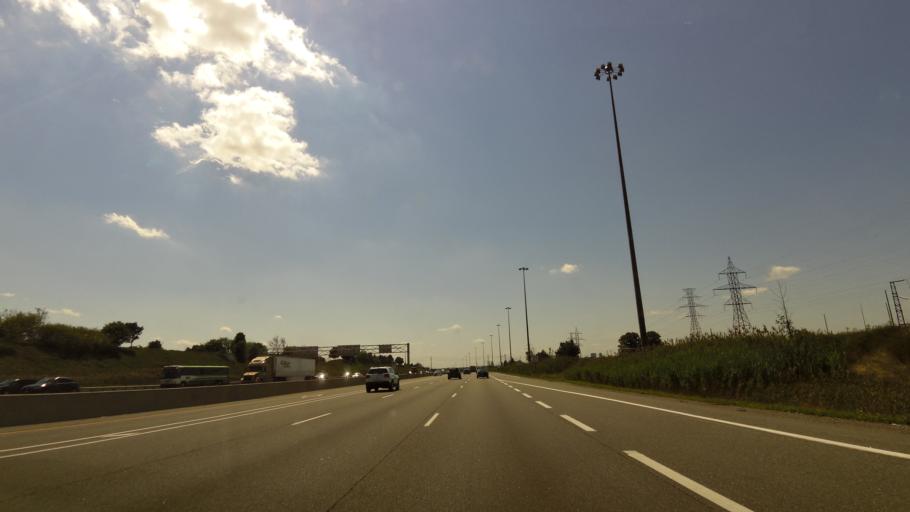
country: CA
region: Ontario
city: Mississauga
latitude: 43.5812
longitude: -79.6655
